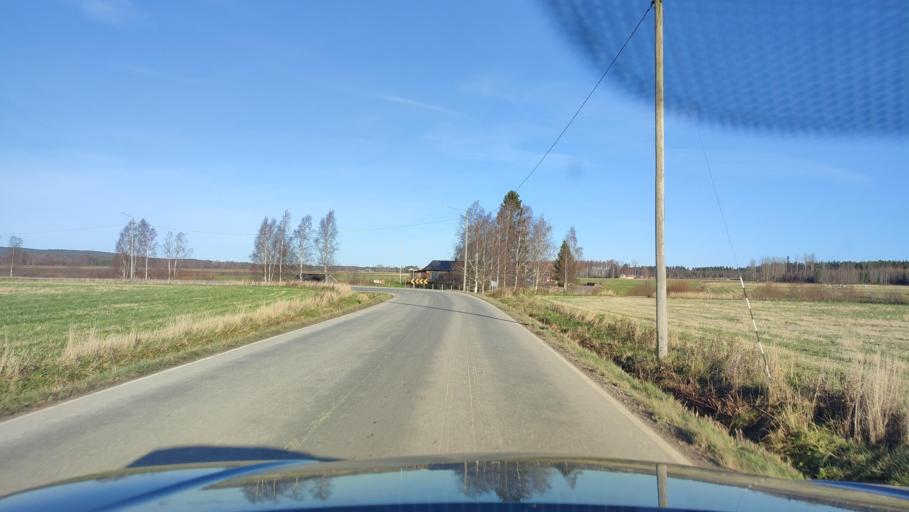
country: FI
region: Southern Ostrobothnia
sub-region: Suupohja
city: Karijoki
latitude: 62.2696
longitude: 21.7248
